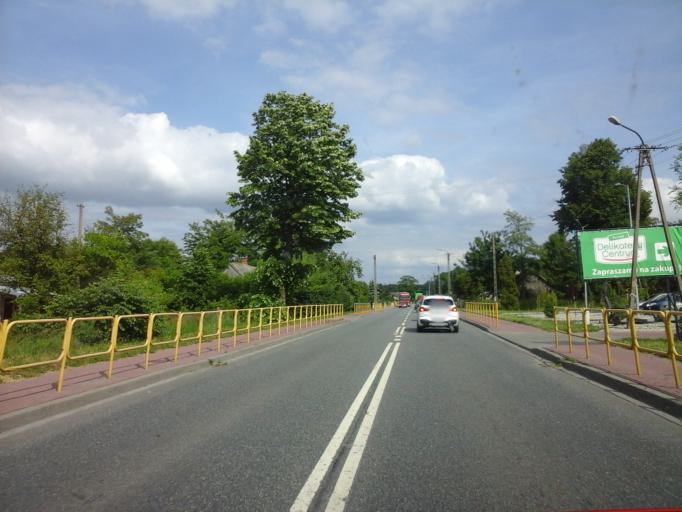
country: PL
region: Lodz Voivodeship
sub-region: Powiat opoczynski
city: Paradyz
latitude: 51.3065
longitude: 20.1098
